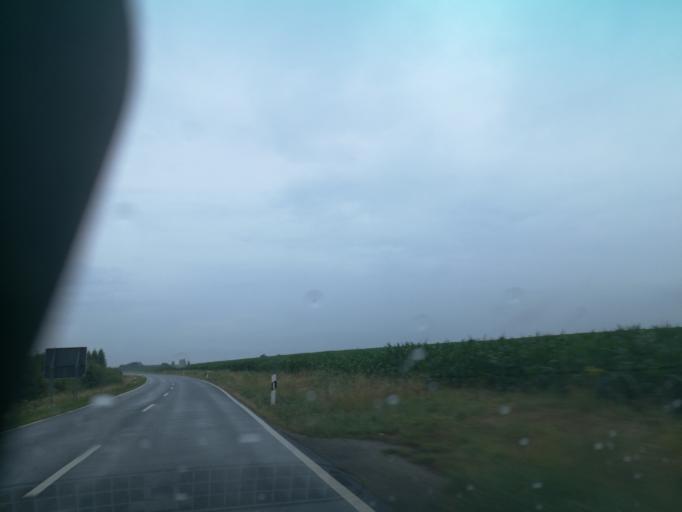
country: DE
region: Bavaria
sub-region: Regierungsbezirk Mittelfranken
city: Obermichelbach
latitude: 49.5308
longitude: 10.9394
